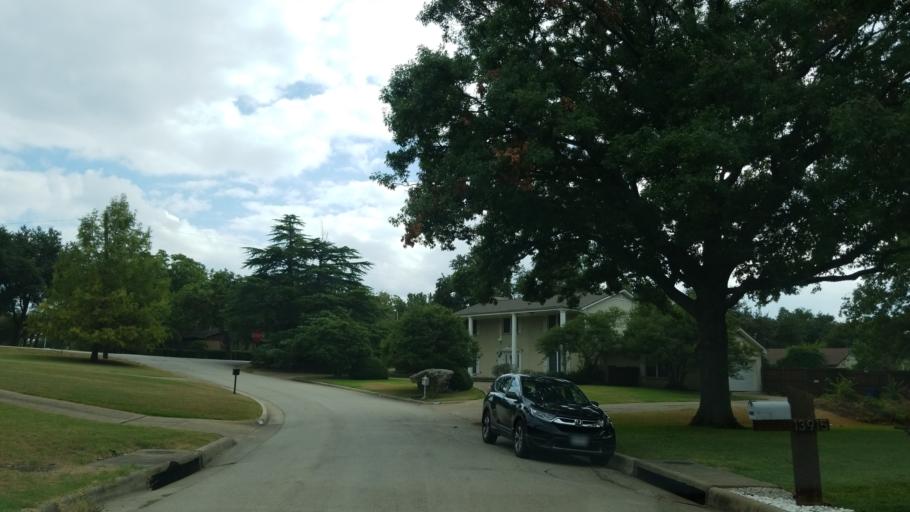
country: US
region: Texas
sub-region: Dallas County
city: Richardson
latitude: 32.9380
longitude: -96.7742
